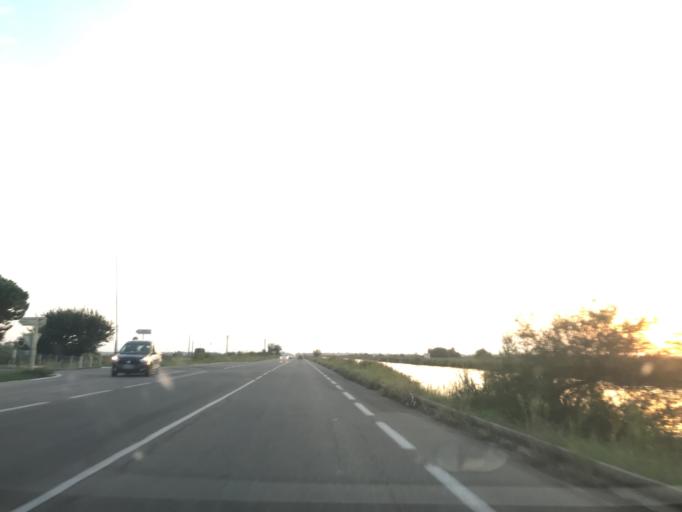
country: FR
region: Languedoc-Roussillon
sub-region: Departement du Gard
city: Aigues-Mortes
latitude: 43.5511
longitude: 4.1686
